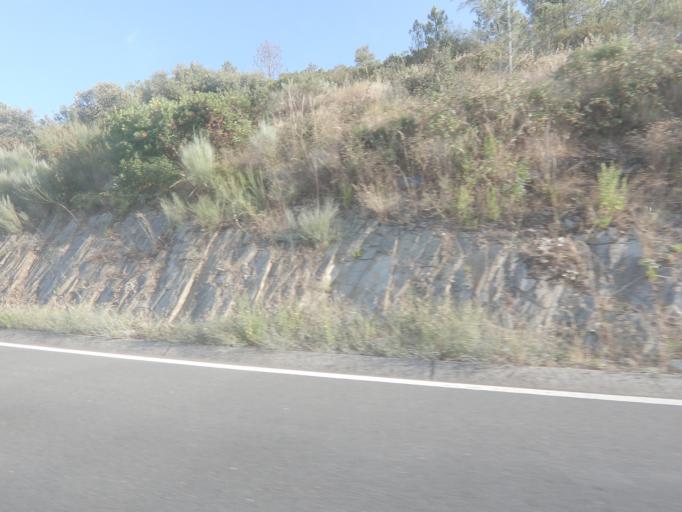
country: PT
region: Viseu
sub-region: Tabuaco
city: Tabuaco
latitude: 41.1500
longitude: -7.6230
